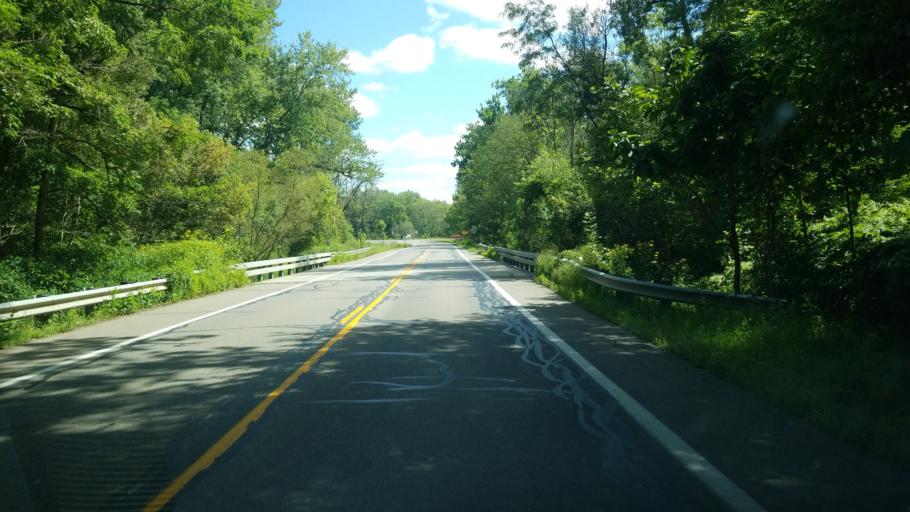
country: US
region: Ohio
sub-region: Ashland County
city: Ashland
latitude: 40.7761
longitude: -82.3720
